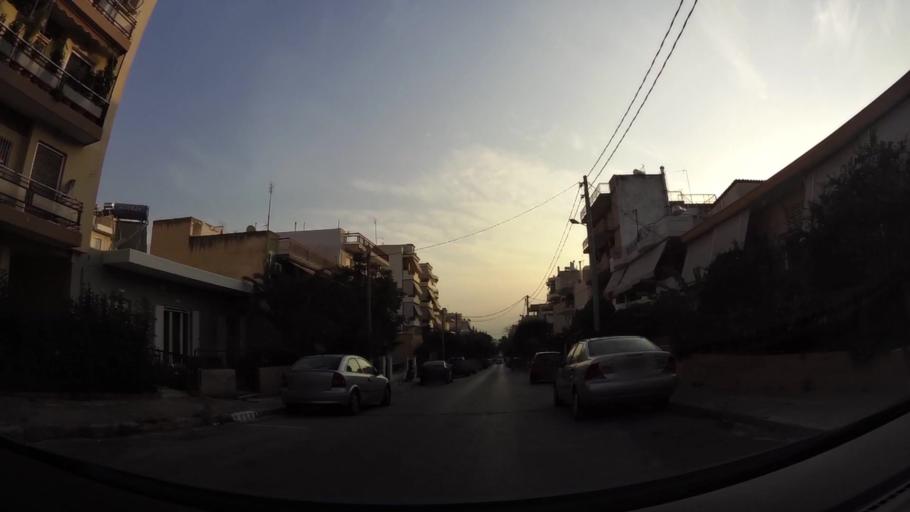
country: GR
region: Attica
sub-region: Nomarchia Athinas
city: Petroupolis
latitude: 38.0423
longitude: 23.6898
